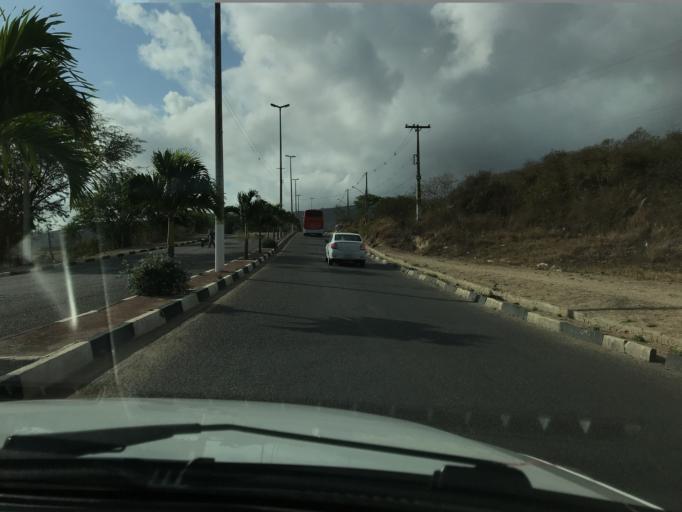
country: BR
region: Pernambuco
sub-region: Bezerros
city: Bezerros
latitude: -8.2347
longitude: -35.7434
